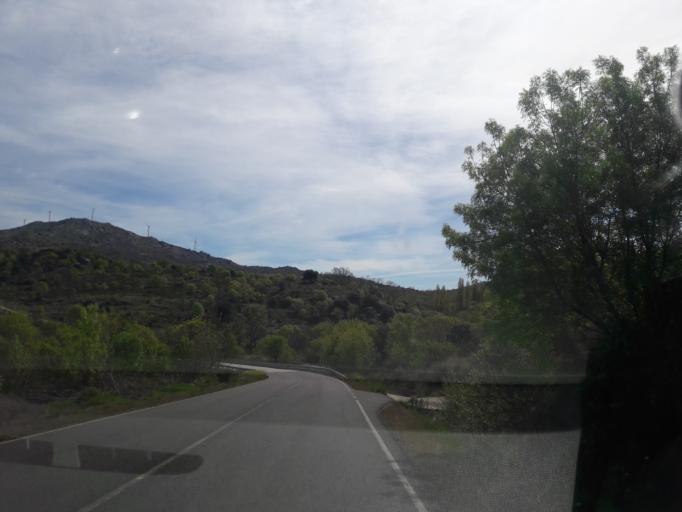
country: ES
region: Castille and Leon
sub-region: Provincia de Salamanca
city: Sanchotello
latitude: 40.4434
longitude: -5.7386
